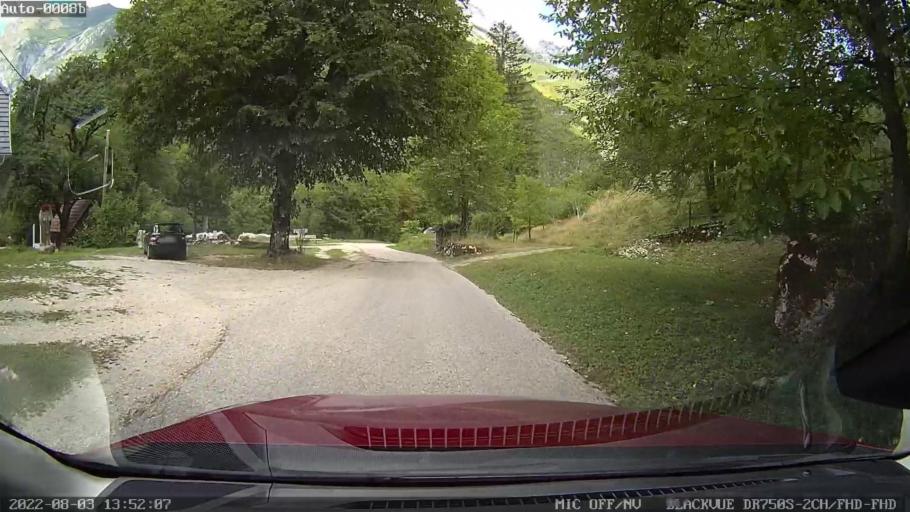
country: SI
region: Bovec
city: Bovec
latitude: 46.3398
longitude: 13.6849
